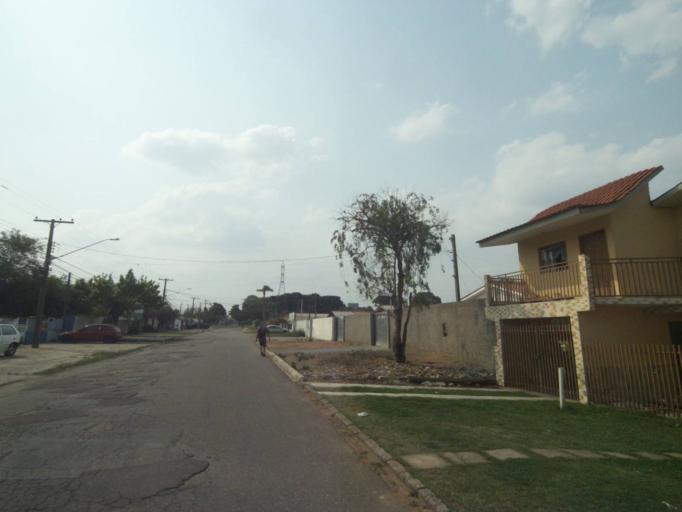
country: BR
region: Parana
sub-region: Sao Jose Dos Pinhais
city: Sao Jose dos Pinhais
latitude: -25.5264
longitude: -49.2310
